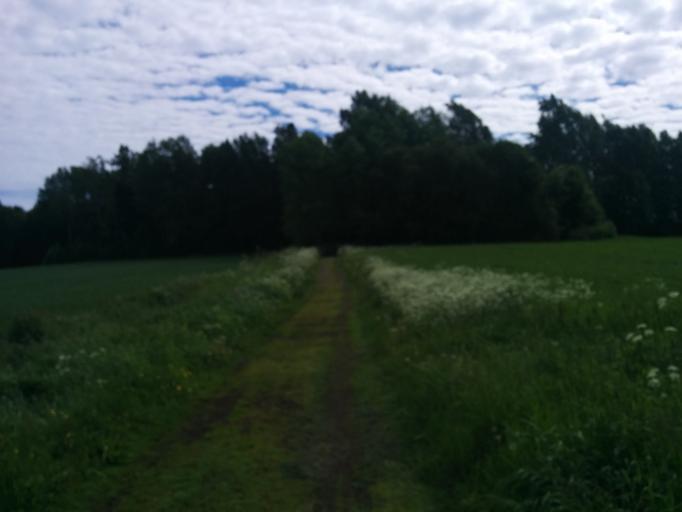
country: FI
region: Uusimaa
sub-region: Helsinki
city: Vantaa
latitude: 60.2377
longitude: 25.1314
